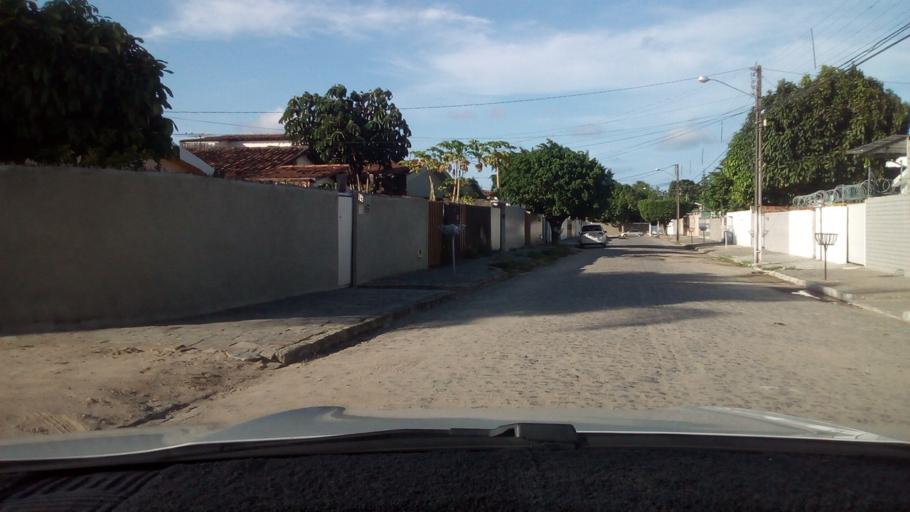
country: BR
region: Paraiba
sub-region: Joao Pessoa
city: Joao Pessoa
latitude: -7.1668
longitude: -34.8552
